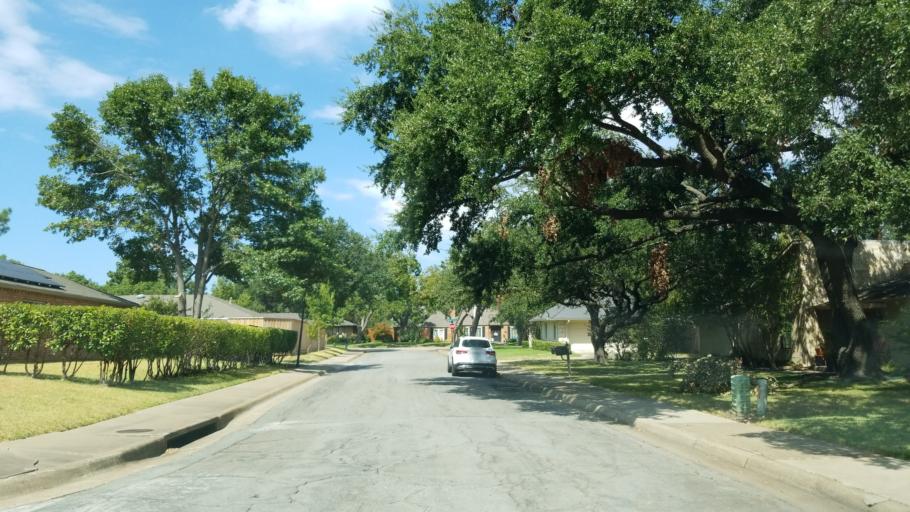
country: US
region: Texas
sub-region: Dallas County
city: Addison
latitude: 32.9562
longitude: -96.7821
